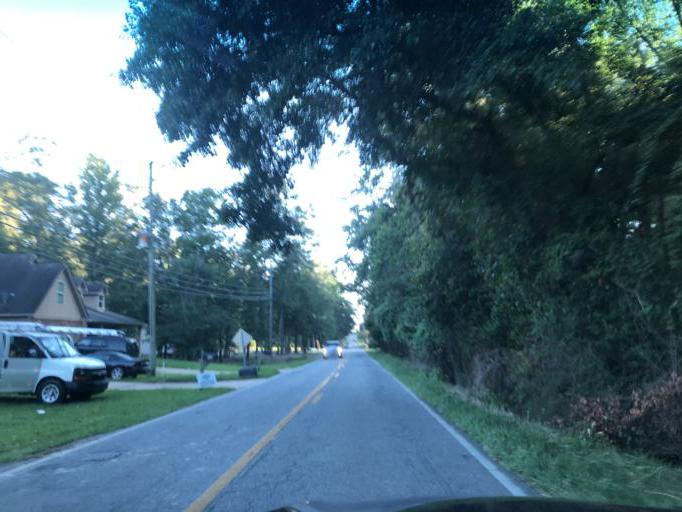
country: US
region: Georgia
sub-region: Muscogee County
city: Columbus
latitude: 32.5315
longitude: -84.8913
